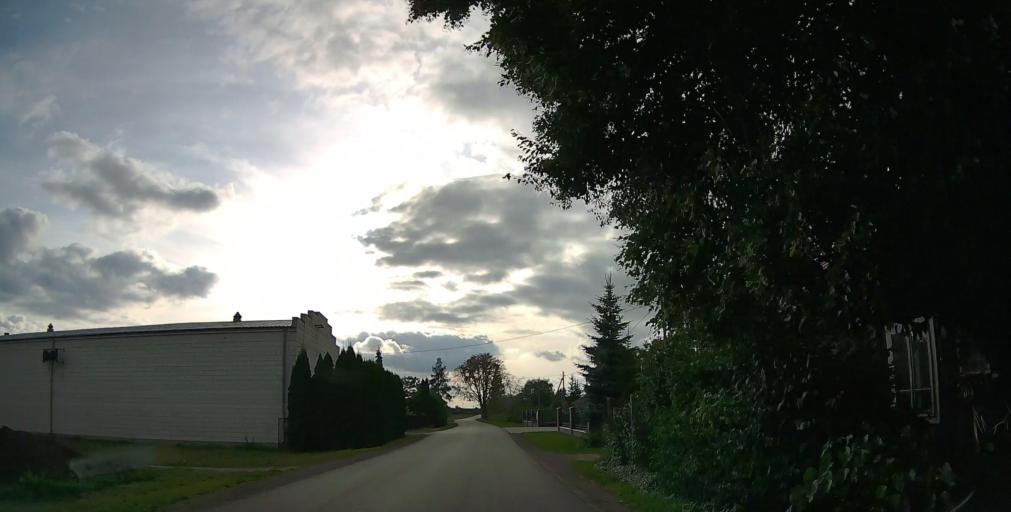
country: PL
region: Masovian Voivodeship
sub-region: Powiat grojecki
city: Jasieniec
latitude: 51.7583
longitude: 20.9348
